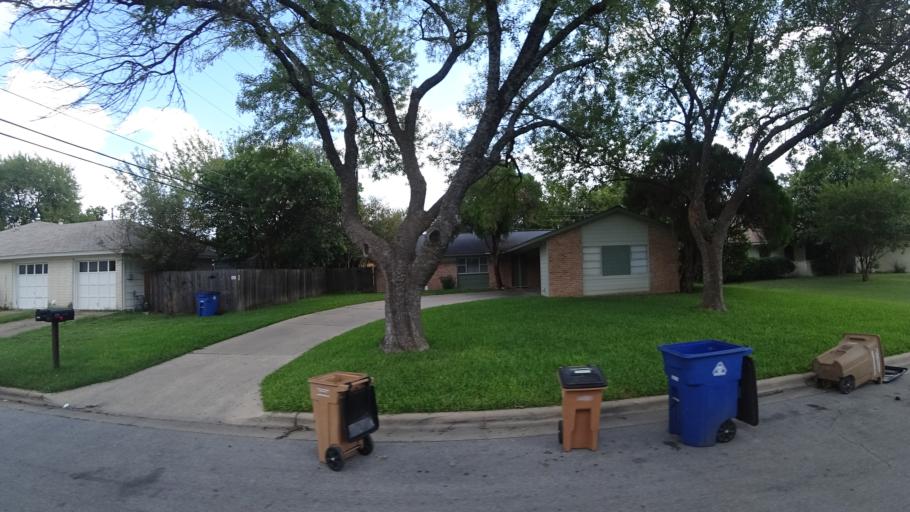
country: US
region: Texas
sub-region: Travis County
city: Austin
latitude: 30.3595
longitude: -97.7285
